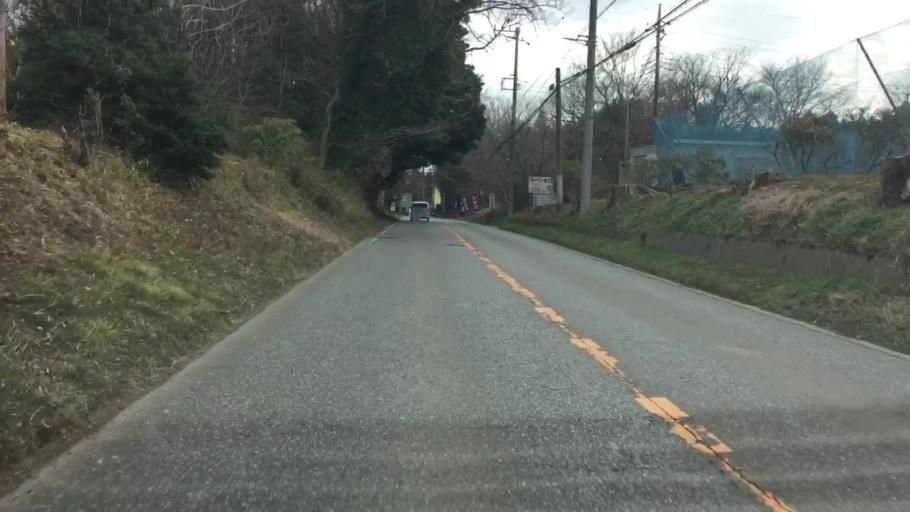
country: JP
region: Ibaraki
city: Ryugasaki
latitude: 35.8211
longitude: 140.1720
